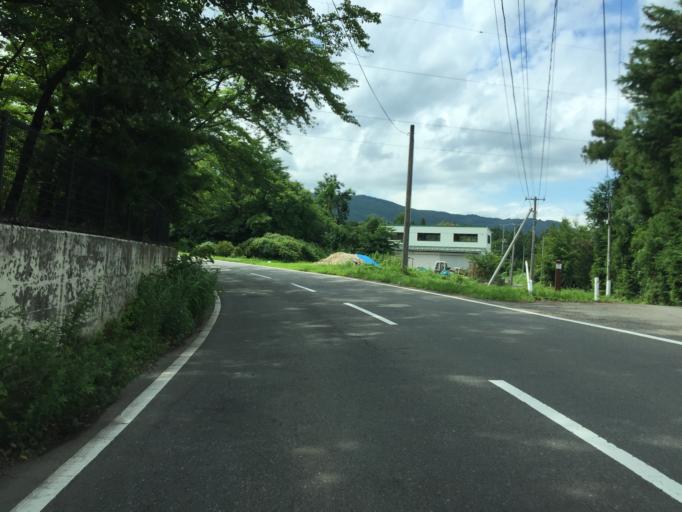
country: JP
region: Fukushima
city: Fukushima-shi
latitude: 37.7088
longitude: 140.3618
